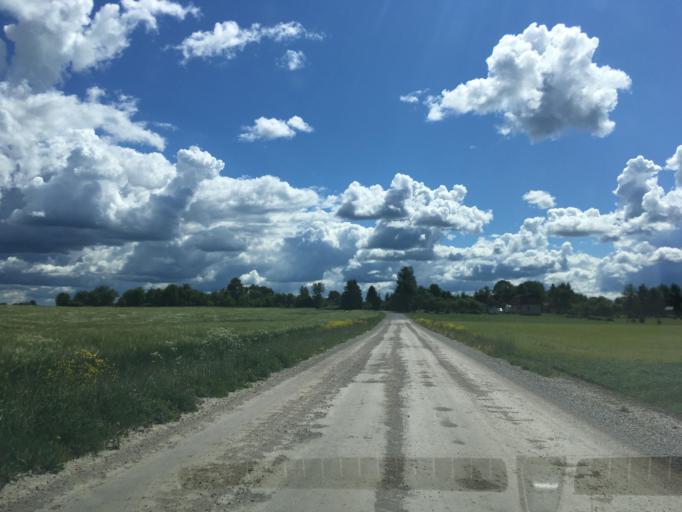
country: EE
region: Harju
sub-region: Nissi vald
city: Turba
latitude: 58.9216
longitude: 24.1603
